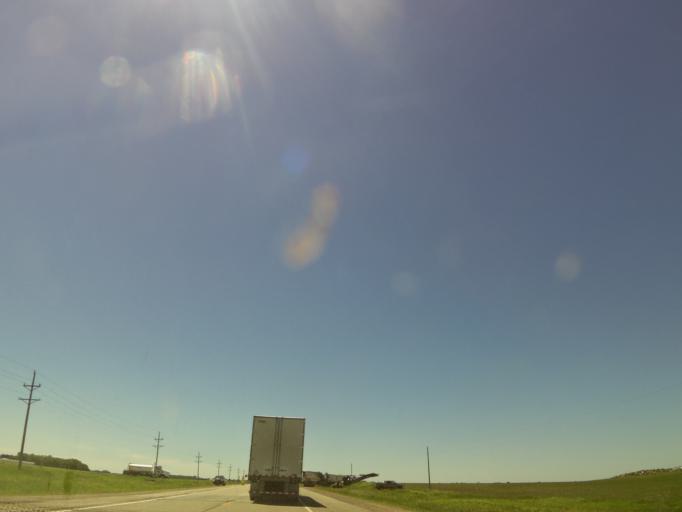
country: US
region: Minnesota
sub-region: Becker County
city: Detroit Lakes
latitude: 47.0155
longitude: -95.9126
